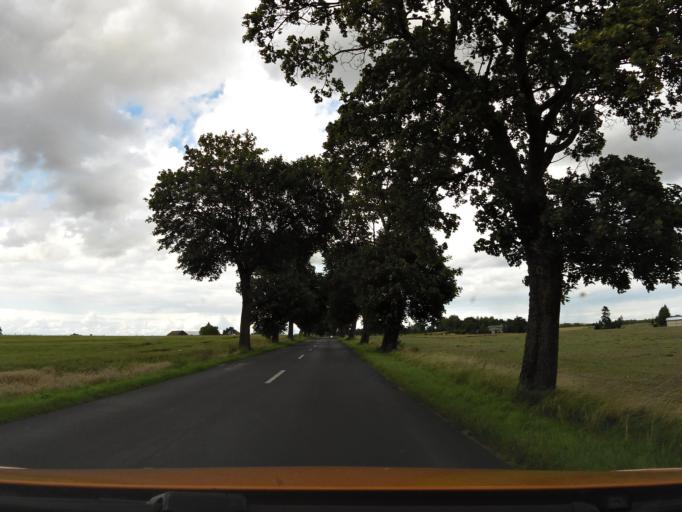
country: PL
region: West Pomeranian Voivodeship
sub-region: Powiat kolobrzeski
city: Ryman
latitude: 54.0421
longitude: 15.5446
